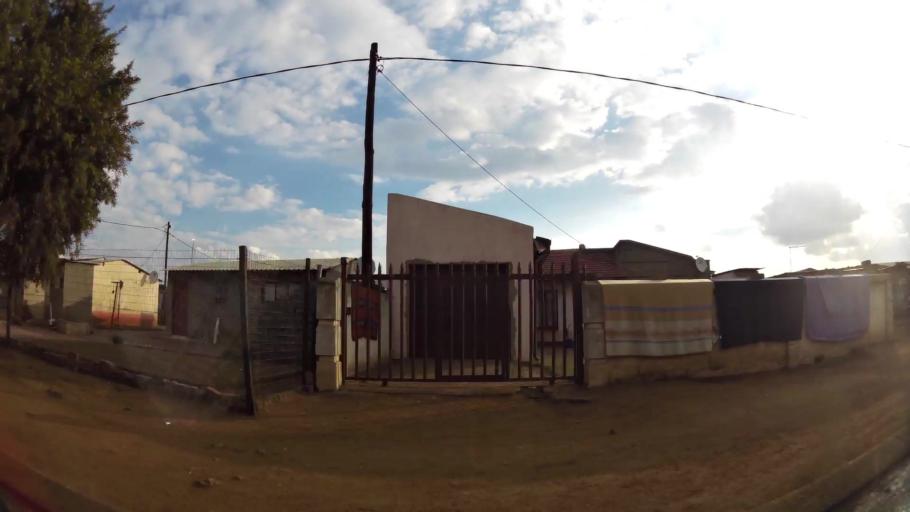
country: ZA
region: Gauteng
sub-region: Sedibeng District Municipality
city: Vanderbijlpark
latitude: -26.6784
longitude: 27.8691
